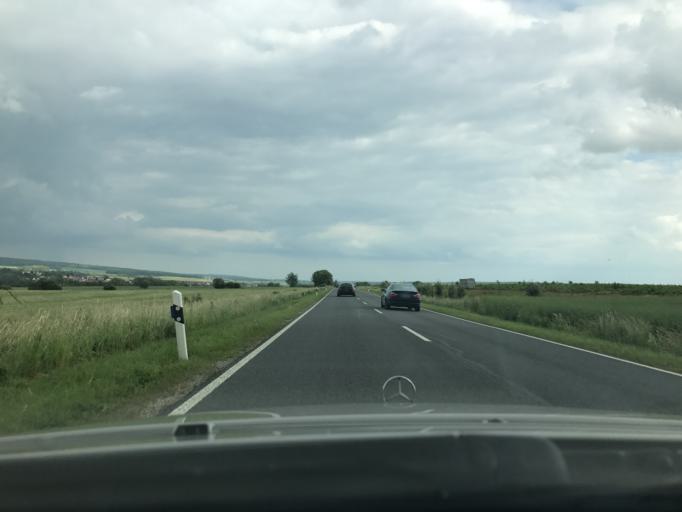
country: DE
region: Thuringia
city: Kefferhausen
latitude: 51.3275
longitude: 10.2951
